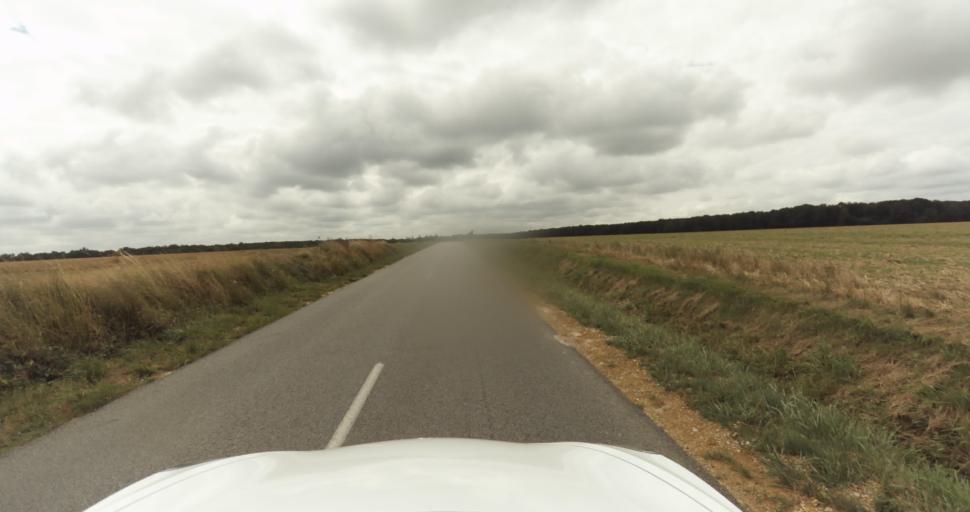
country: FR
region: Haute-Normandie
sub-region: Departement de l'Eure
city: Claville
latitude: 49.0122
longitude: 1.0340
